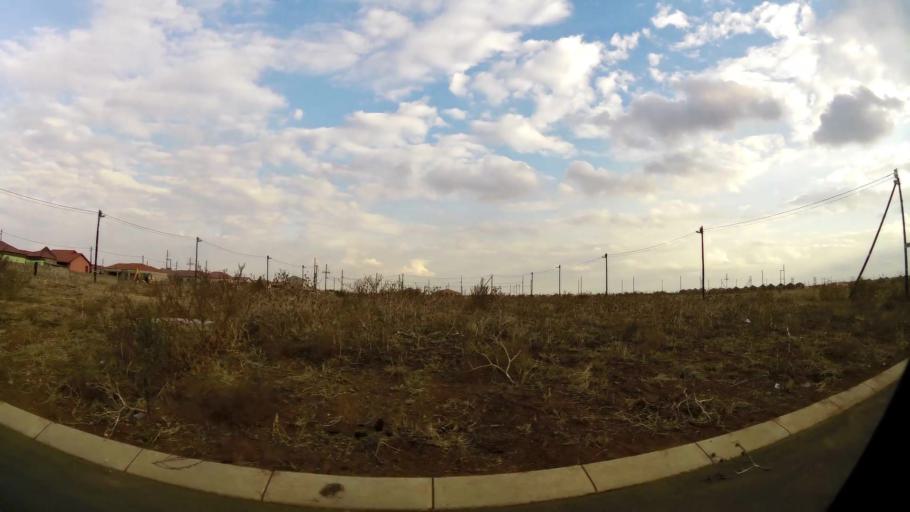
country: ZA
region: Gauteng
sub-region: Sedibeng District Municipality
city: Vanderbijlpark
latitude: -26.6075
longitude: 27.8117
